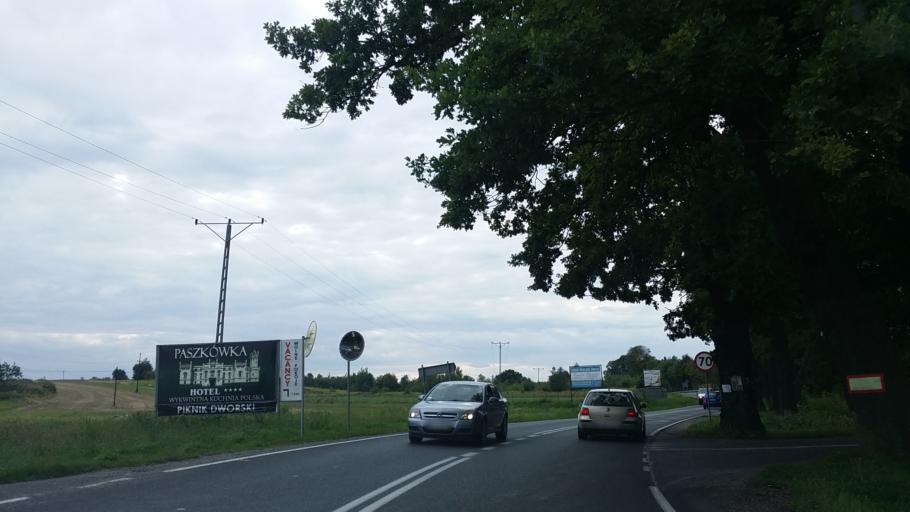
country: PL
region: Lesser Poland Voivodeship
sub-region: Powiat wadowicki
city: Sosnowice
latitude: 49.9590
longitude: 19.7018
